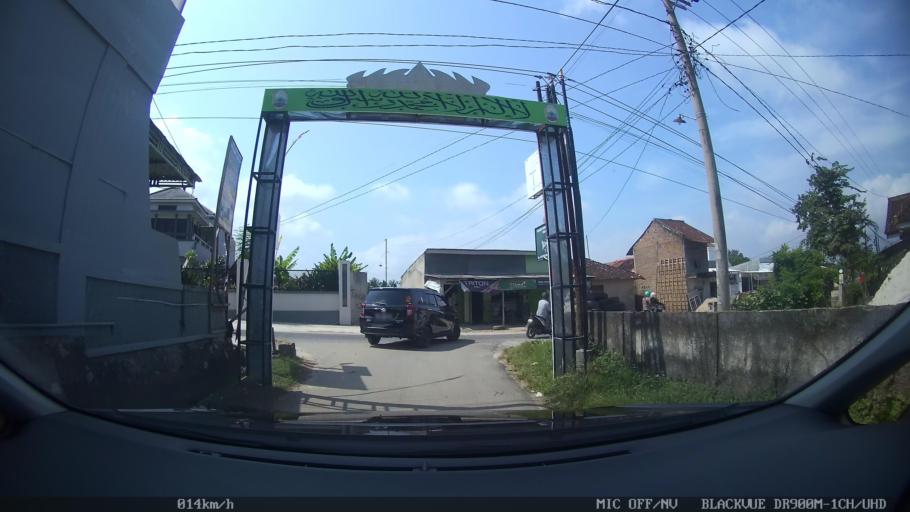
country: ID
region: Lampung
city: Kedaton
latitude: -5.3419
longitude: 105.2713
